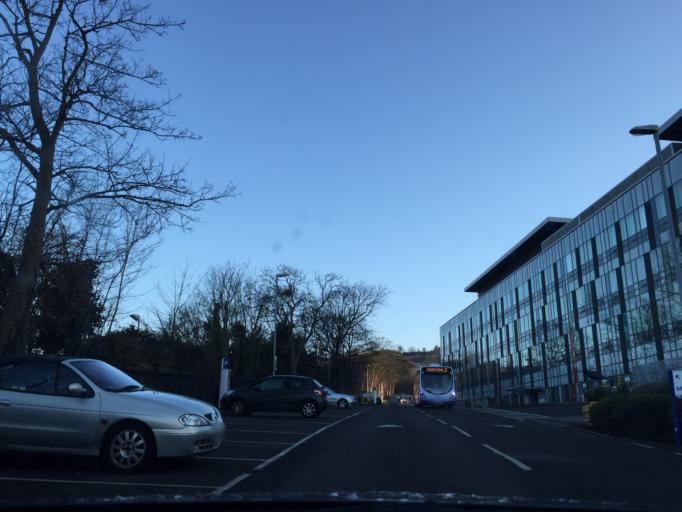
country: GB
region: England
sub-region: Portsmouth
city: Cosham
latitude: 50.8495
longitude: -1.0718
